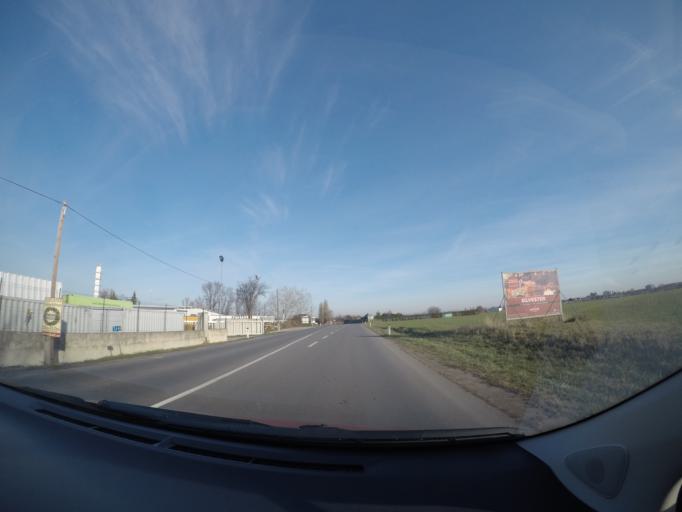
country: AT
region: Lower Austria
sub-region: Politischer Bezirk Baden
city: Traiskirchen
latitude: 48.0302
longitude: 16.2894
